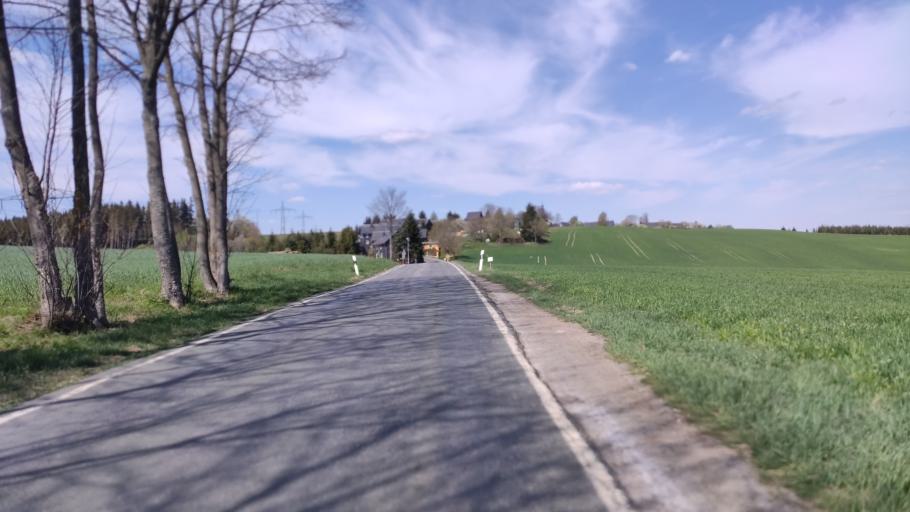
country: DE
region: Thuringia
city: Leutenberg
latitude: 50.5098
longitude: 11.4515
